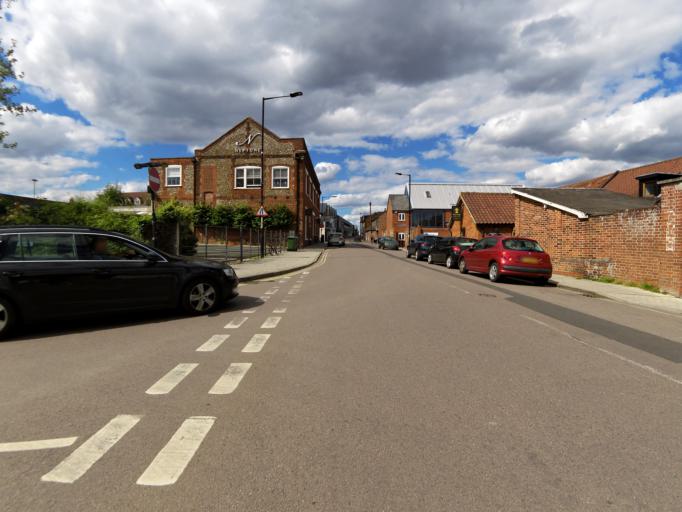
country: GB
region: England
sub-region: Suffolk
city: Bury St Edmunds
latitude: 52.2437
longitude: 0.7111
